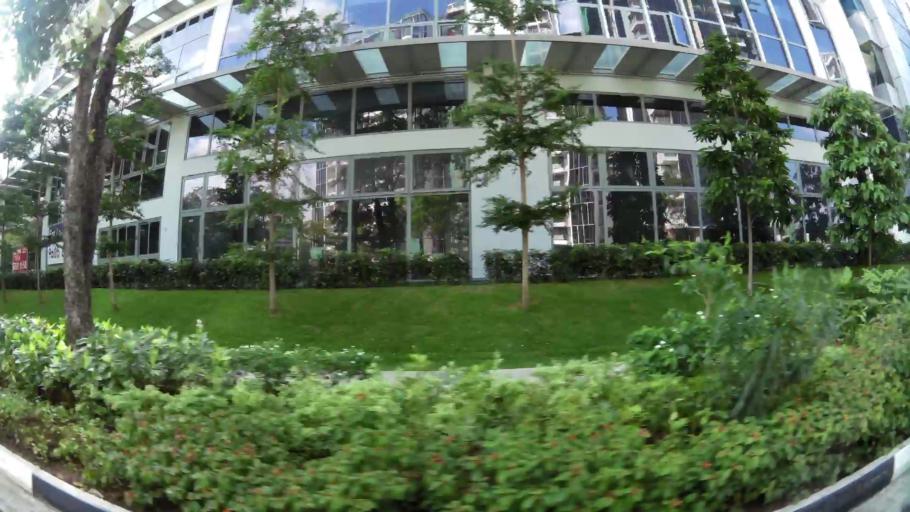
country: SG
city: Singapore
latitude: 1.3184
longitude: 103.8811
